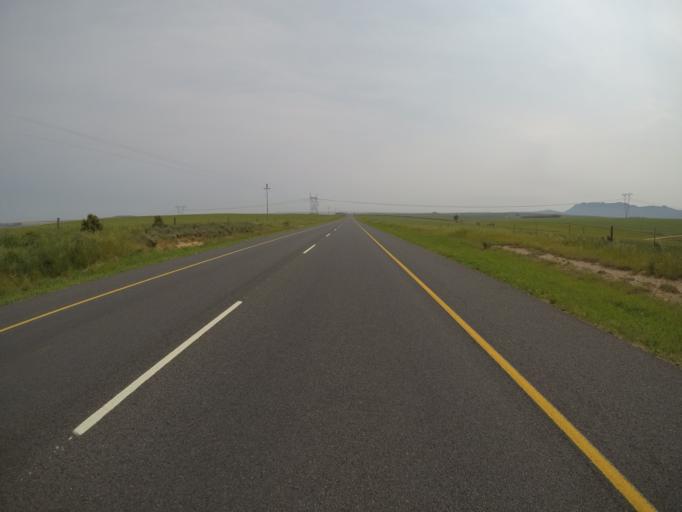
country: ZA
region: Western Cape
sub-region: West Coast District Municipality
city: Malmesbury
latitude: -33.4951
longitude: 18.8285
